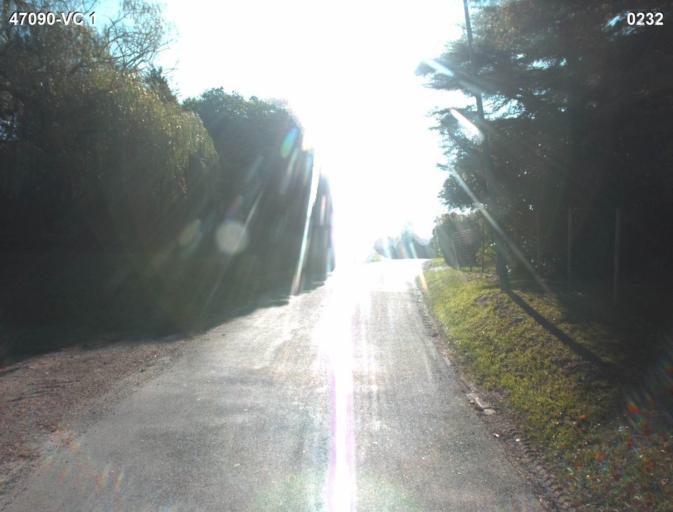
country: FR
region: Aquitaine
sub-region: Departement du Lot-et-Garonne
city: Nerac
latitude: 44.1695
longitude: 0.3751
